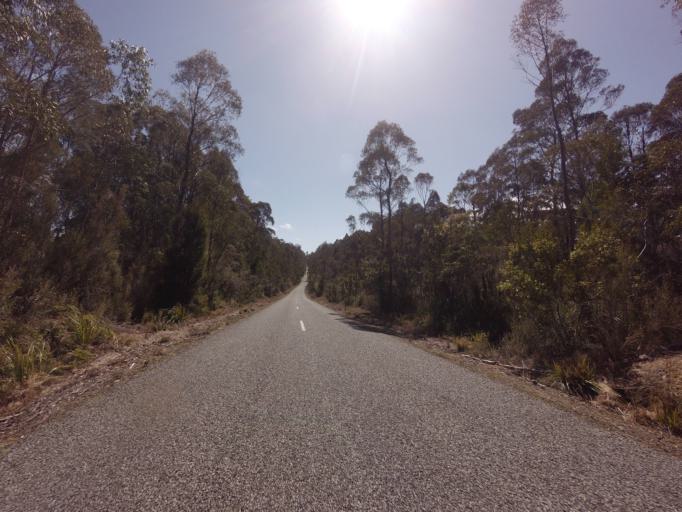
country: AU
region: Tasmania
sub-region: Derwent Valley
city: New Norfolk
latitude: -42.7535
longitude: 146.4106
